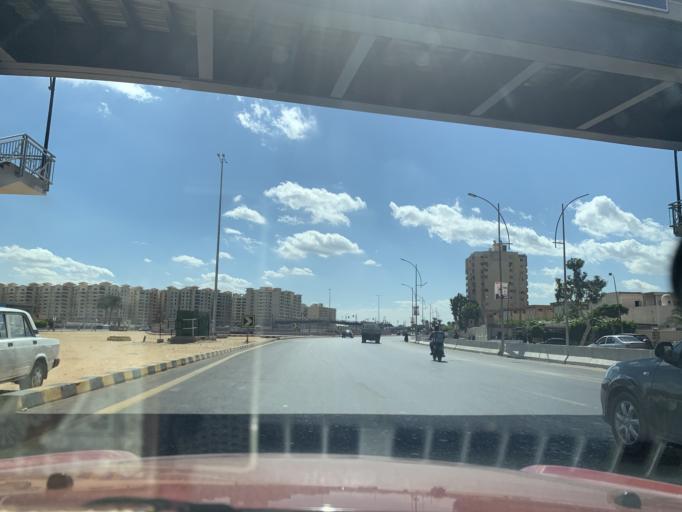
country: EG
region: Alexandria
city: Alexandria
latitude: 31.2070
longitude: 29.9547
